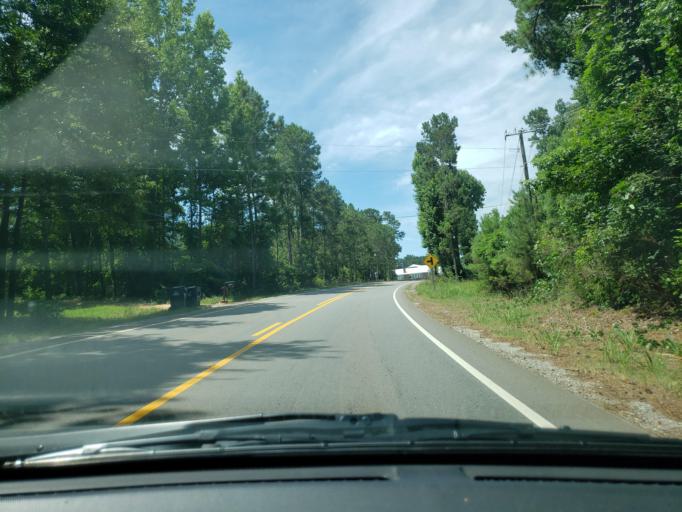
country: US
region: Alabama
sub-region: Elmore County
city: Eclectic
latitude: 32.6751
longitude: -85.9447
